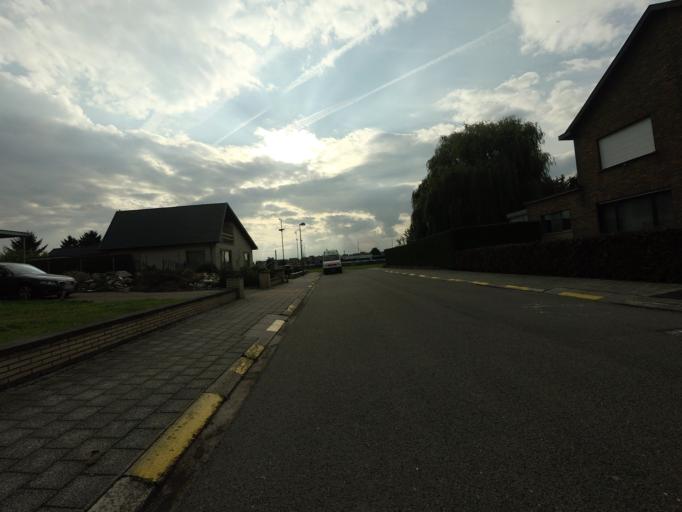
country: BE
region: Flanders
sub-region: Provincie Vlaams-Brabant
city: Kapelle-op-den-Bos
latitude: 51.0136
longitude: 4.3396
